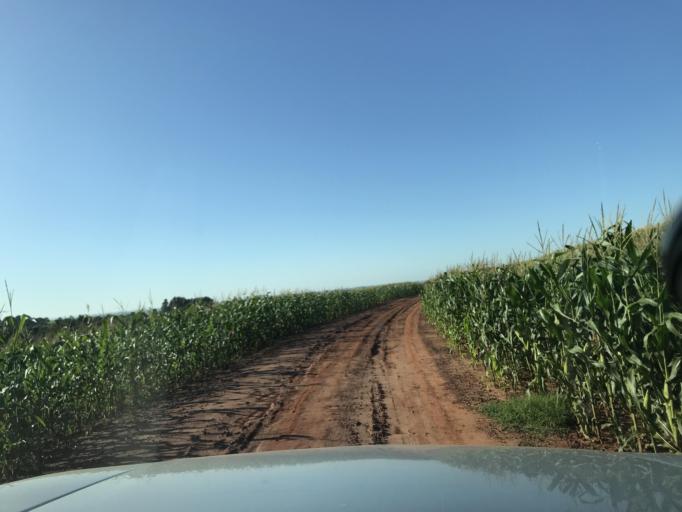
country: BR
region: Parana
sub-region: Palotina
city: Palotina
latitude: -24.2339
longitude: -53.7739
